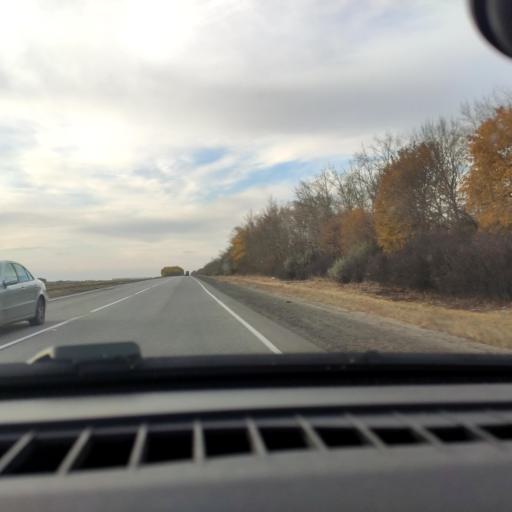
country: RU
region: Voronezj
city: Ostrogozhsk
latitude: 50.9502
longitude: 39.0483
